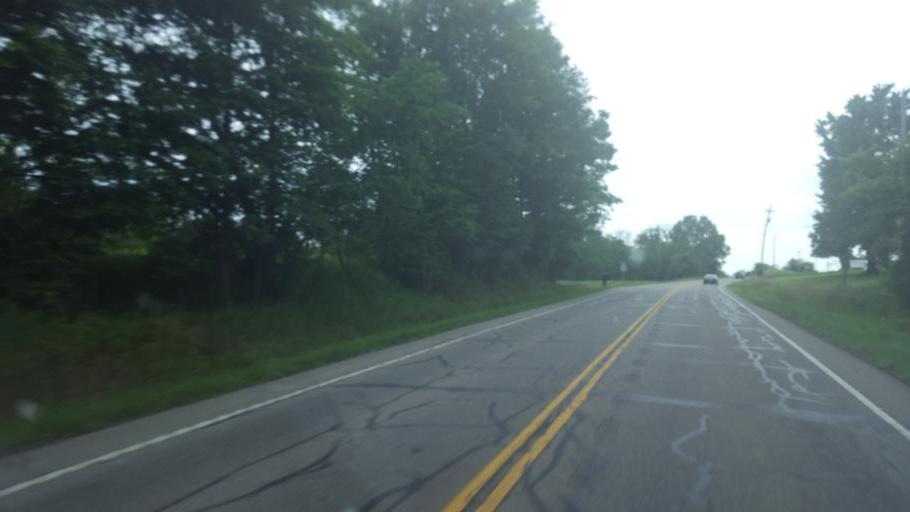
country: US
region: Ohio
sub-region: Richland County
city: Lincoln Heights
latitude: 40.8954
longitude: -82.5044
